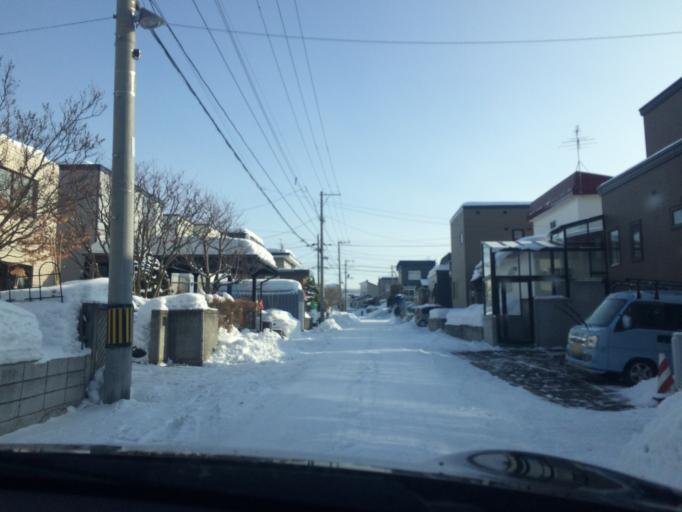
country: JP
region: Hokkaido
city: Ebetsu
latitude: 43.0416
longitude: 141.4900
